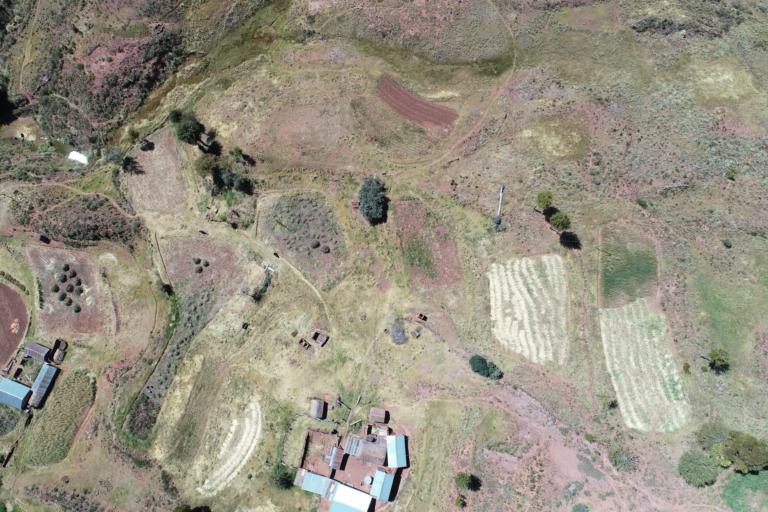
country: BO
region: La Paz
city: Tiahuanaco
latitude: -16.6070
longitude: -68.7640
